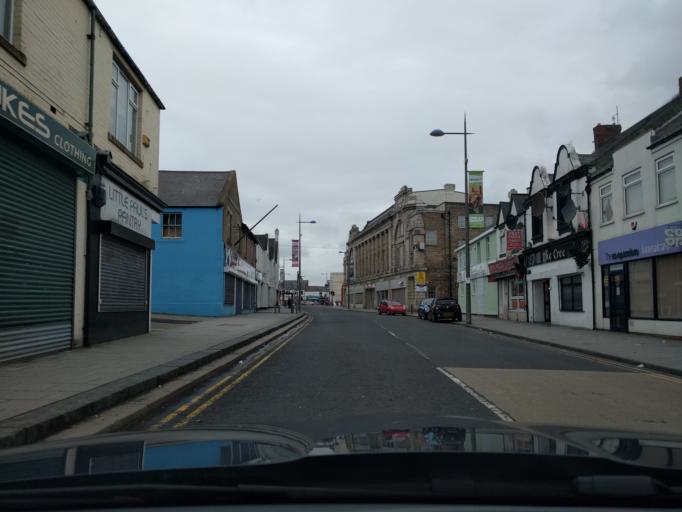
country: GB
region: England
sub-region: Northumberland
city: Ashington
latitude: 55.1838
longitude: -1.5657
